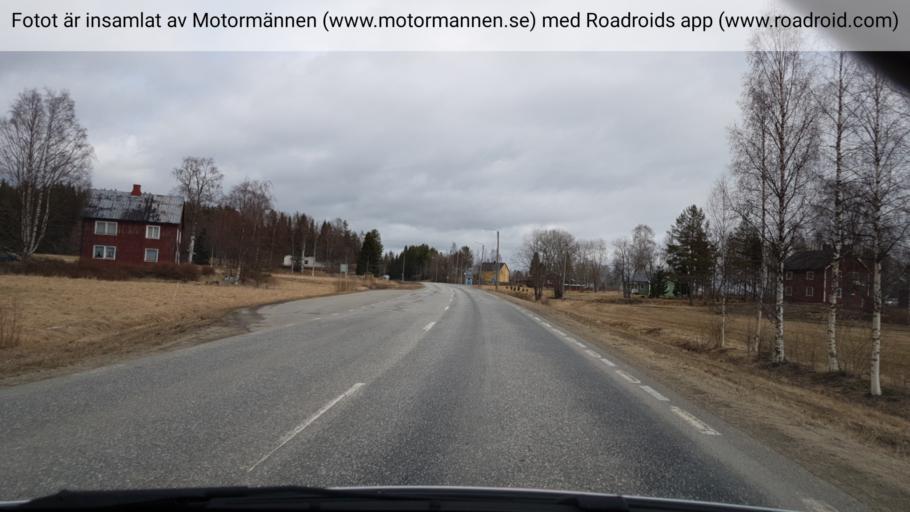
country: SE
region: Vaesterbotten
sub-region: Bjurholms Kommun
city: Bjurholm
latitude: 63.9158
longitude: 19.1727
